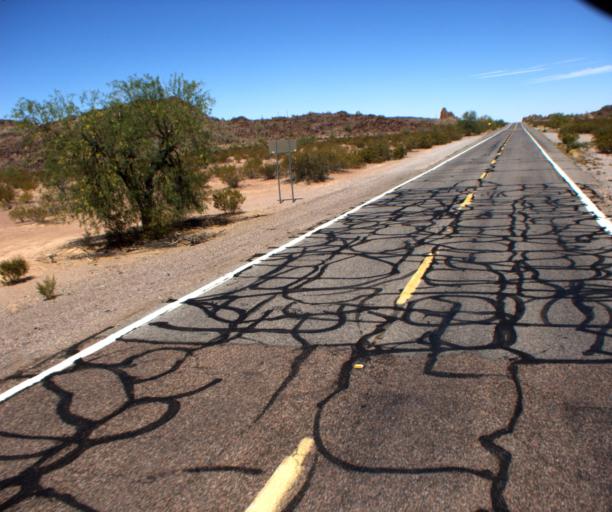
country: US
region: Arizona
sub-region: Pima County
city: Ajo
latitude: 32.5347
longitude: -112.8801
